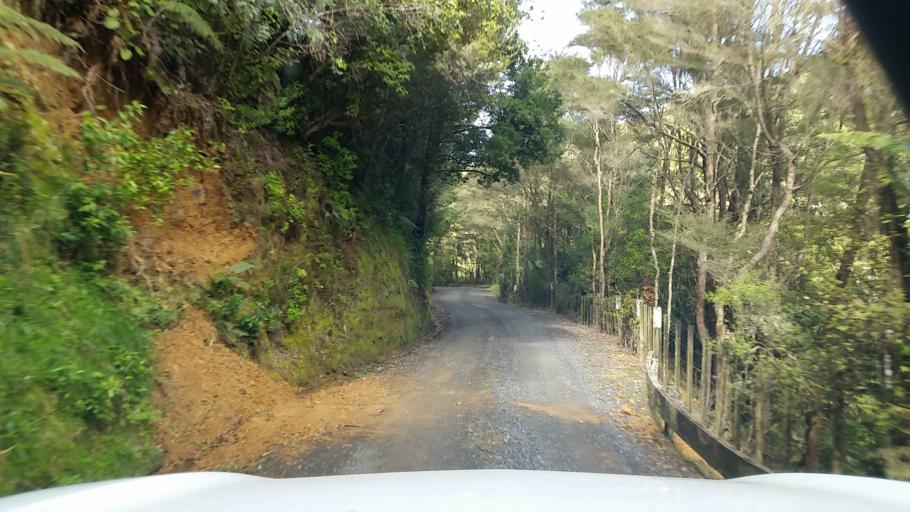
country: NZ
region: Waikato
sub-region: Hauraki District
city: Ngatea
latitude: -37.4694
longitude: 175.4552
